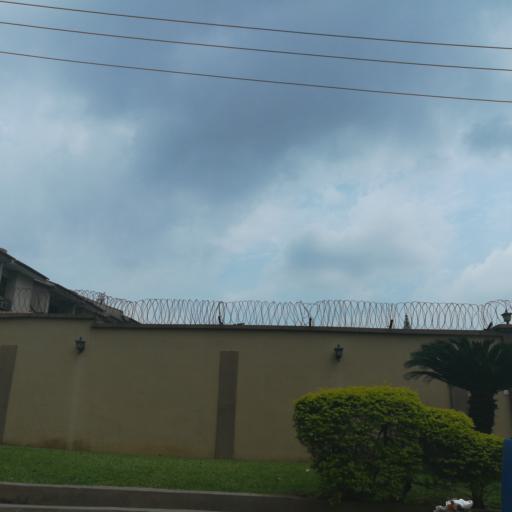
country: NG
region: Lagos
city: Ojota
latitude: 6.5790
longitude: 3.3809
